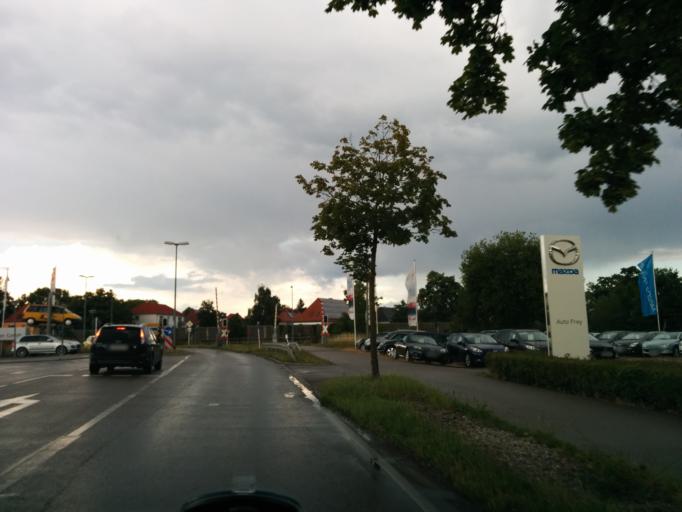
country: DE
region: Bavaria
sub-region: Swabia
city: Klosterlechfeld
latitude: 48.1728
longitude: 10.8381
